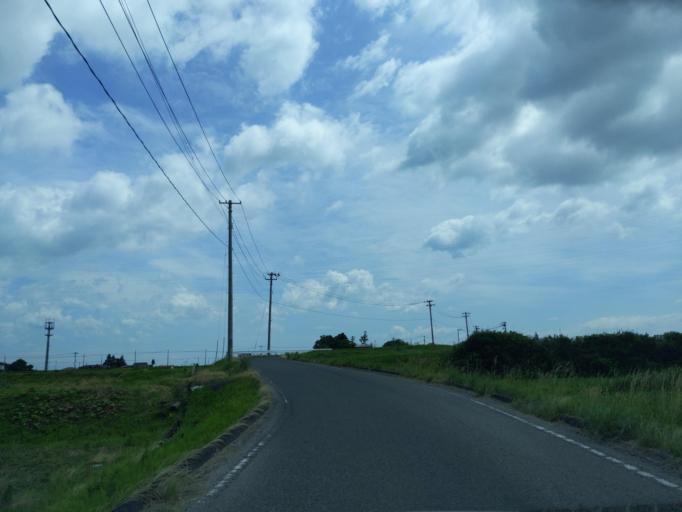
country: JP
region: Fukushima
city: Koriyama
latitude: 37.4401
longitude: 140.3550
